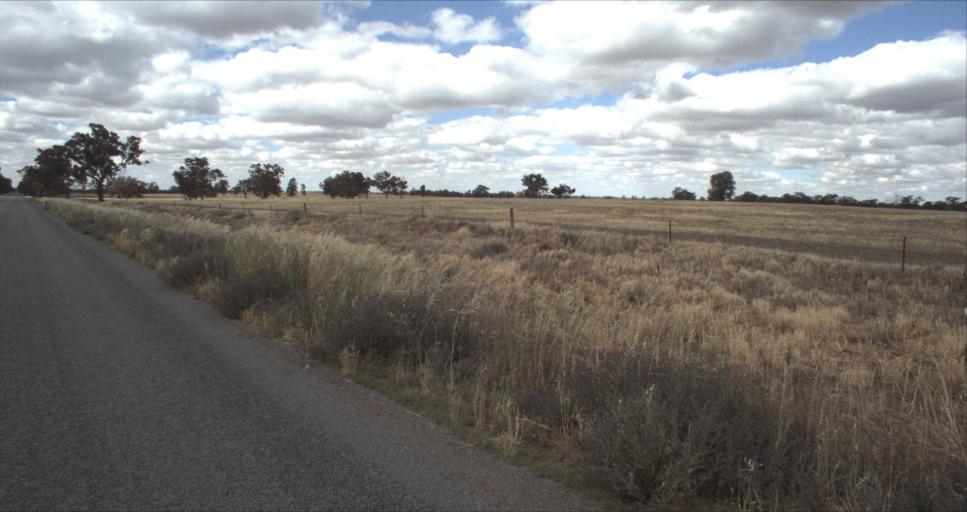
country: AU
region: New South Wales
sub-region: Leeton
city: Leeton
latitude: -34.6897
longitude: 146.3440
